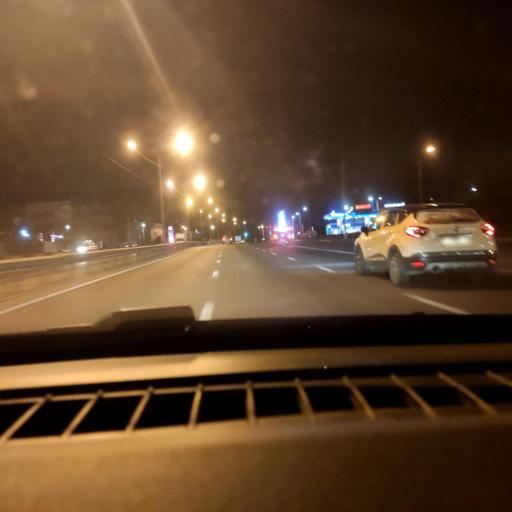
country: RU
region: Voronezj
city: Pridonskoy
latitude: 51.6686
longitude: 39.1244
